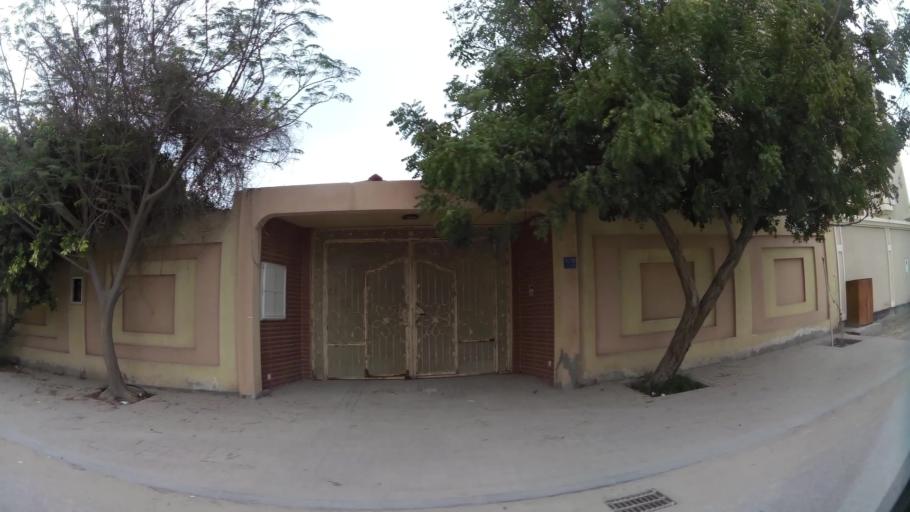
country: BH
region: Northern
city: Sitrah
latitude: 26.1701
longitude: 50.6075
